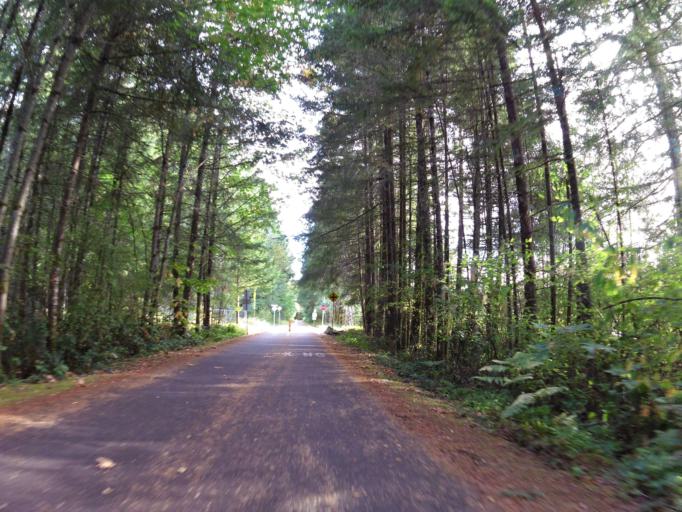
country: US
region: Washington
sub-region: Thurston County
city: Tenino
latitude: 46.9387
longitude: -122.8226
